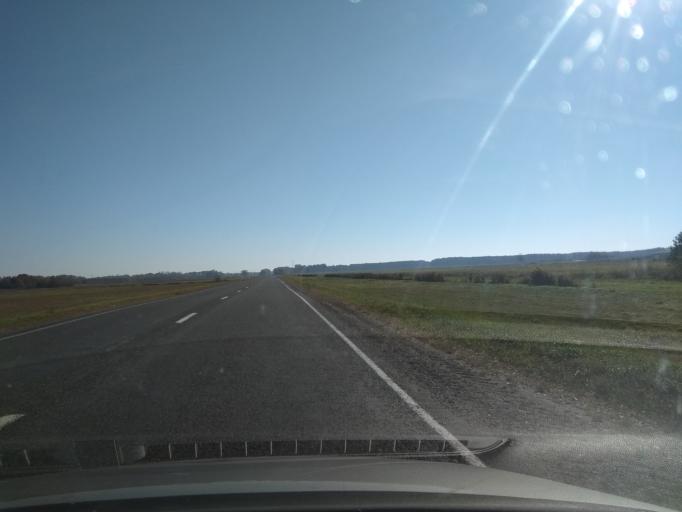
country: BY
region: Brest
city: Malaryta
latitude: 51.9434
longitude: 24.0276
